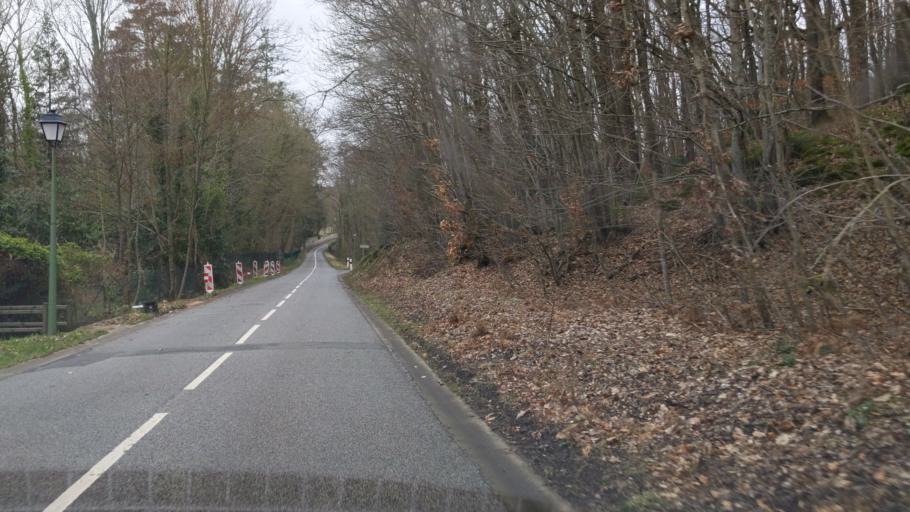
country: FR
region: Ile-de-France
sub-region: Departement des Yvelines
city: Chevreuse
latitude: 48.6857
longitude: 2.0227
